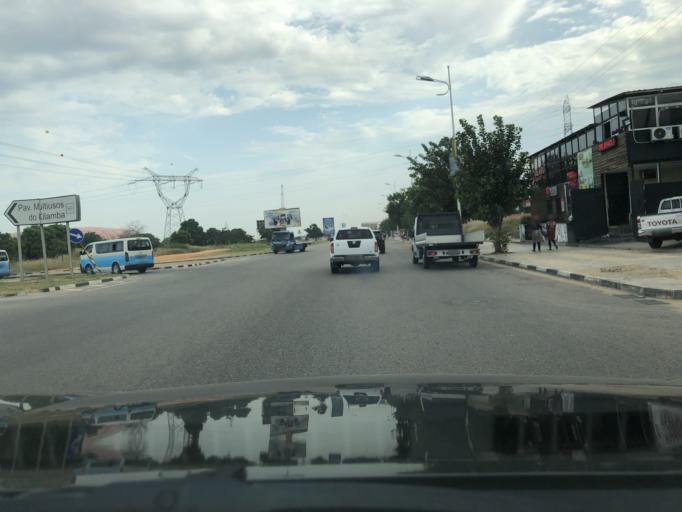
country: AO
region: Luanda
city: Luanda
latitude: -8.9760
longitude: 13.2895
